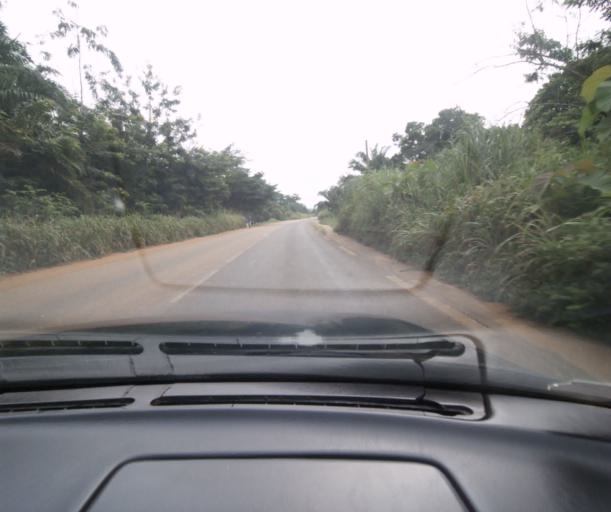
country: CM
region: Centre
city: Ombesa
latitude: 4.4119
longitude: 11.2481
